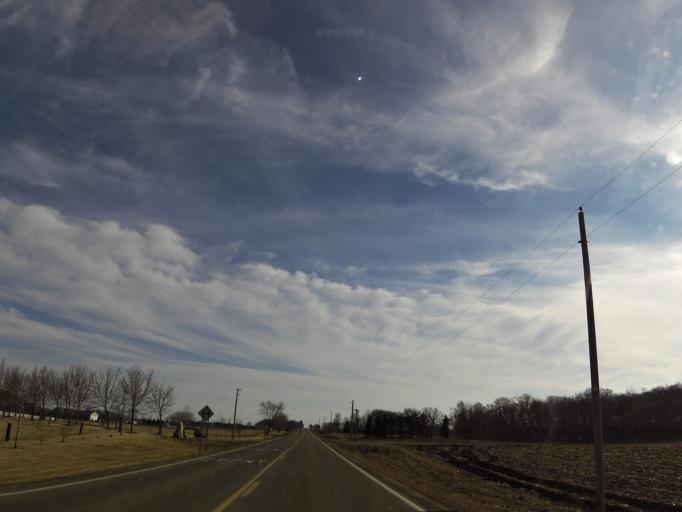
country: US
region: Minnesota
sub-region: Rice County
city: Northfield
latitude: 44.5417
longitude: -93.2009
